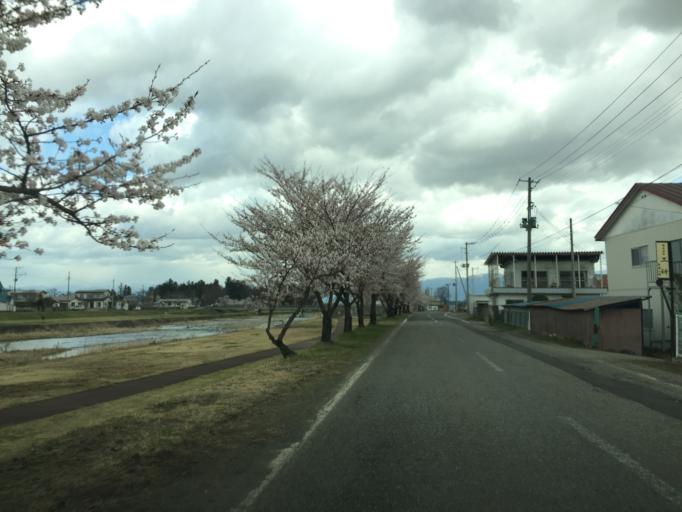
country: JP
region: Fukushima
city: Kitakata
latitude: 37.4500
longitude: 139.8384
